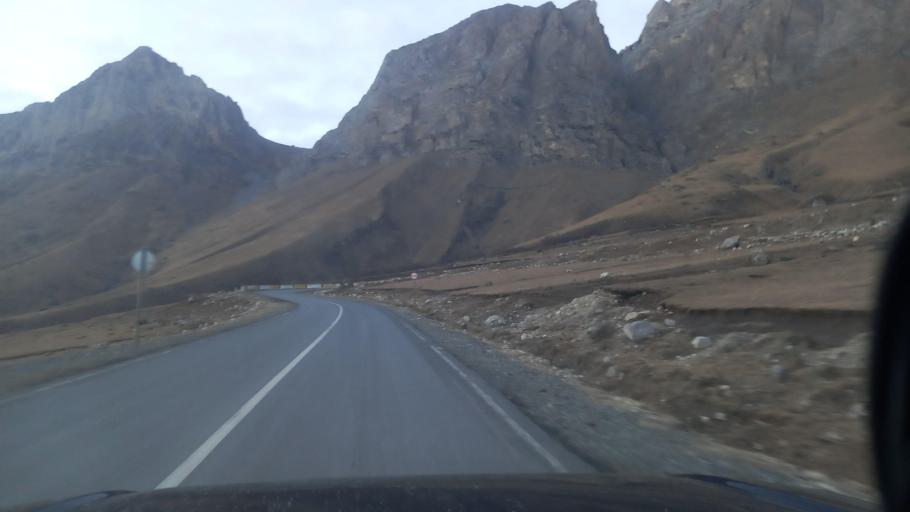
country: RU
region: Ingushetiya
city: Dzhayrakh
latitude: 42.8239
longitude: 44.8248
